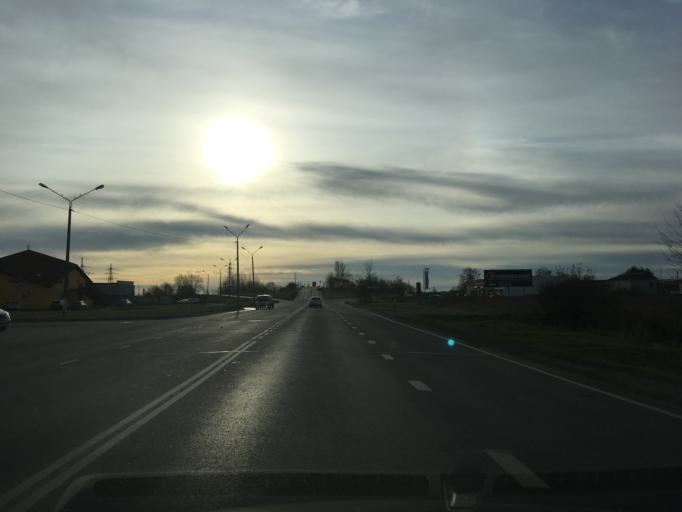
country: EE
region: Ida-Virumaa
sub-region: Narva linn
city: Narva
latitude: 59.3756
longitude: 28.1544
